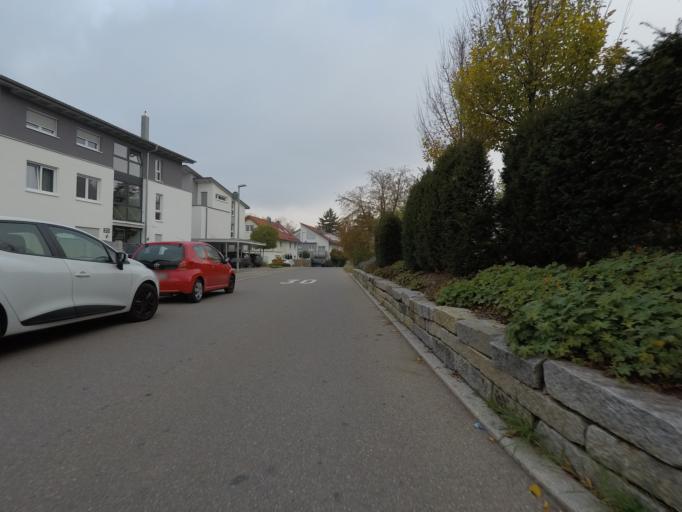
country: DE
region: Baden-Wuerttemberg
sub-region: Tuebingen Region
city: Pfullingen
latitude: 48.4875
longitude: 9.2305
